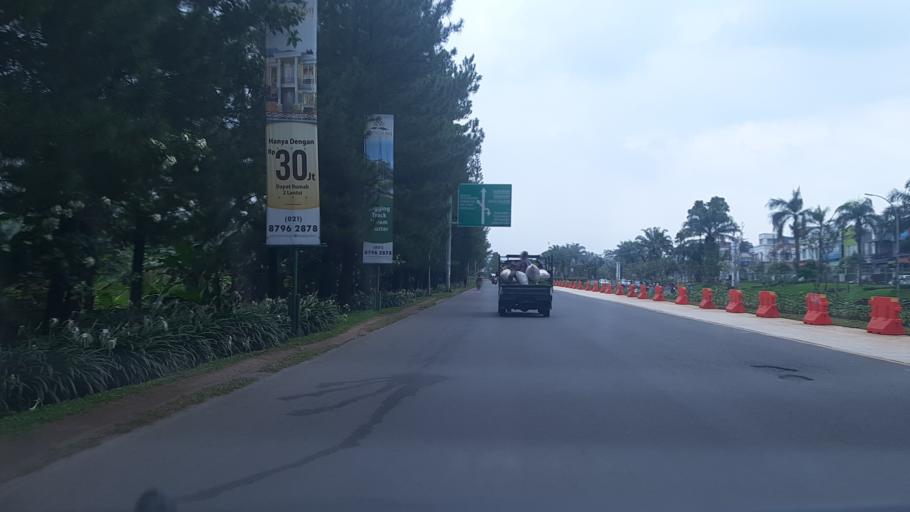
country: ID
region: West Java
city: Bogor
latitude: -6.5696
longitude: 106.8618
